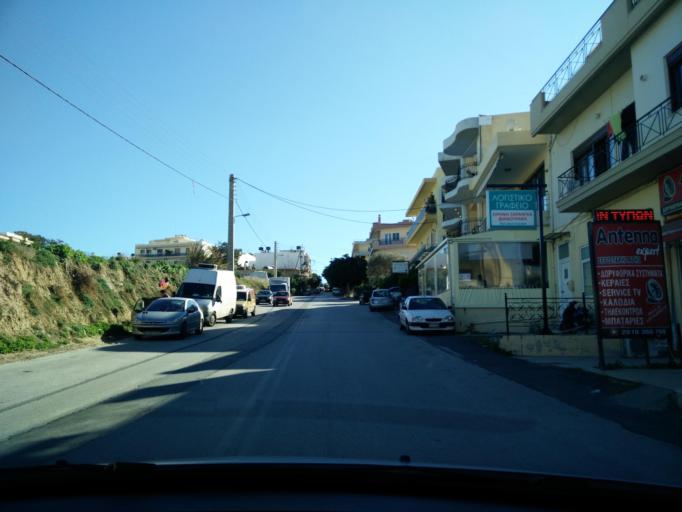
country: GR
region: Crete
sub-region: Nomos Irakleiou
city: Irakleion
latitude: 35.3303
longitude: 25.1407
